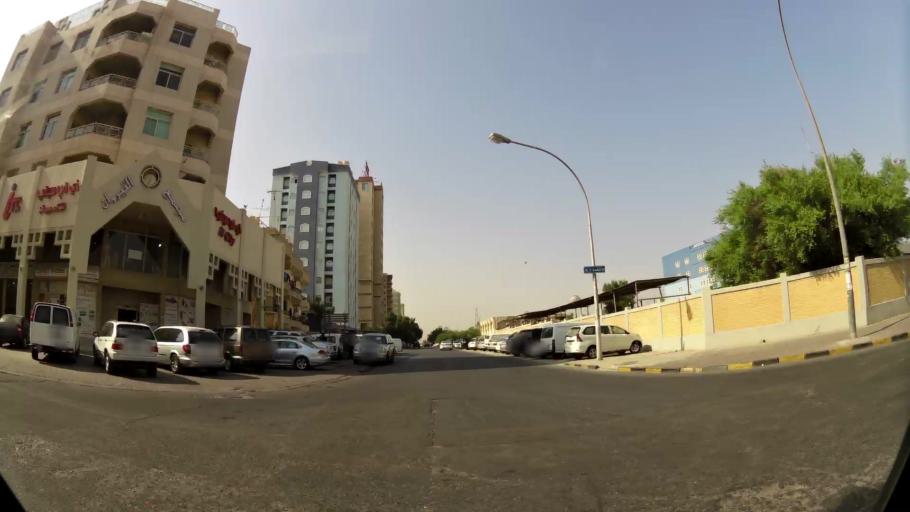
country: KW
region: Muhafazat Hawalli
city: Hawalli
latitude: 29.3418
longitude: 48.0089
